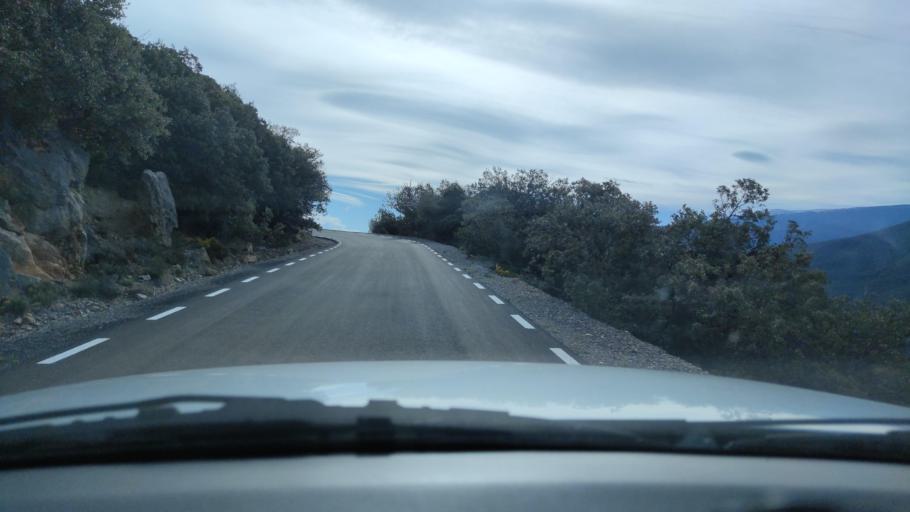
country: ES
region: Catalonia
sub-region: Provincia de Lleida
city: Coll de Nargo
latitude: 42.2411
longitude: 1.4077
